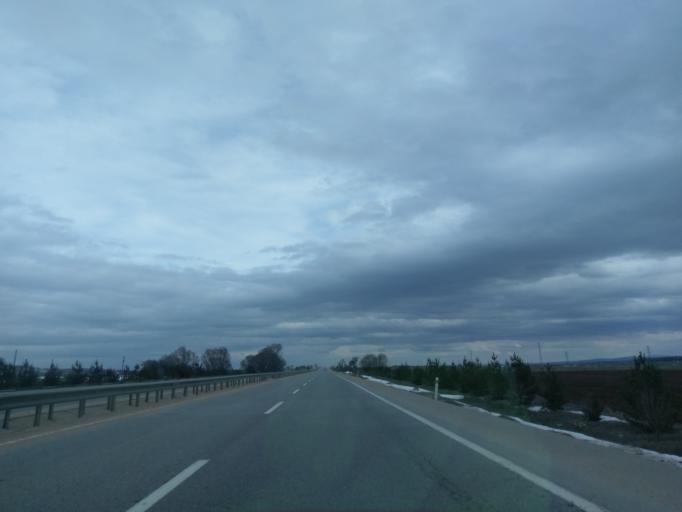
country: TR
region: Eskisehir
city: Inonu
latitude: 39.7199
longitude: 30.2185
